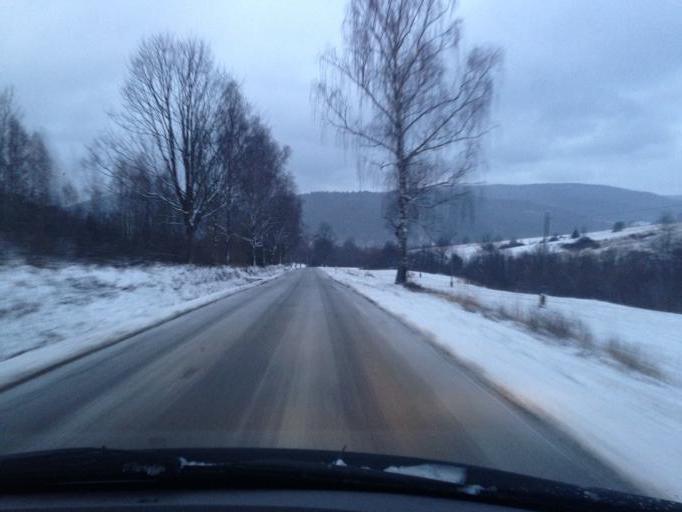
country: PL
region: Subcarpathian Voivodeship
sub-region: Powiat jasielski
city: Krempna
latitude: 49.5215
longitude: 21.5021
